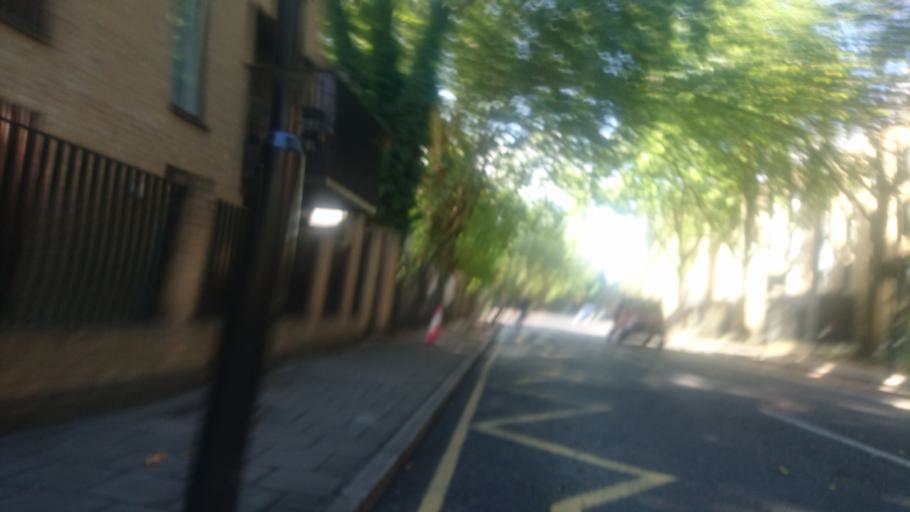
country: GB
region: England
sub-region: Greater London
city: Islington
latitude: 51.5450
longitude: -0.1017
